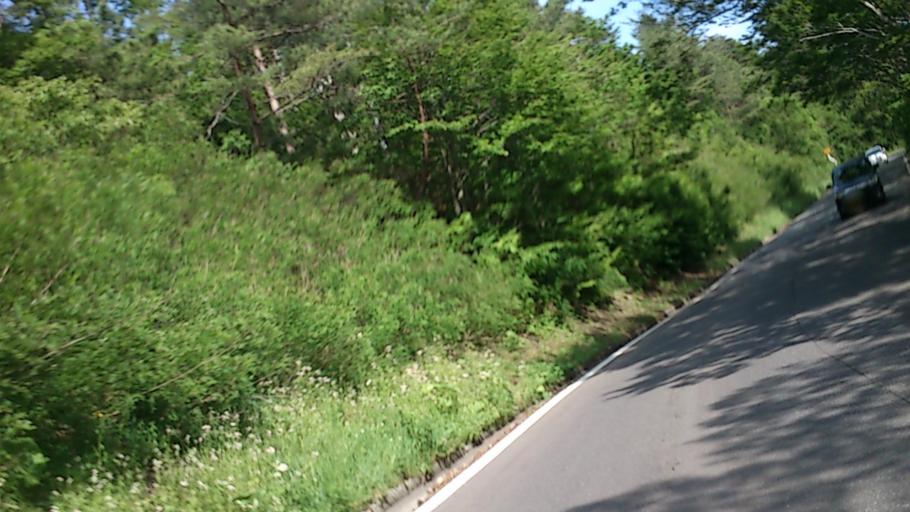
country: JP
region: Aomori
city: Aomori Shi
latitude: 40.7147
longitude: 140.8200
